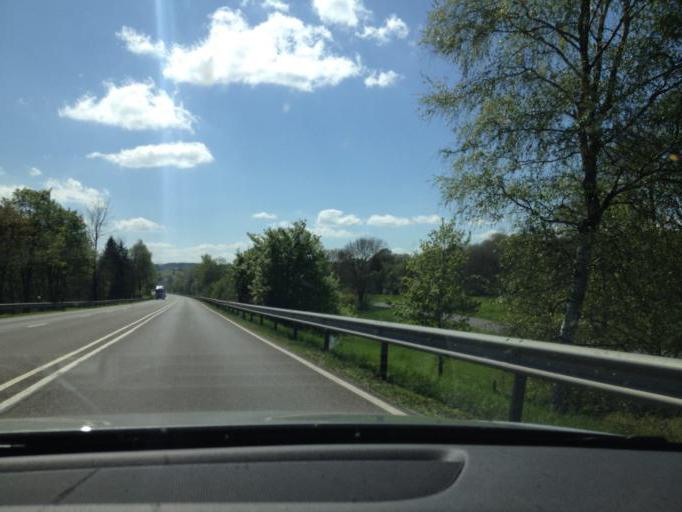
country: DE
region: Rheinland-Pfalz
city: Neuendorf
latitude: 50.2873
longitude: 6.4713
